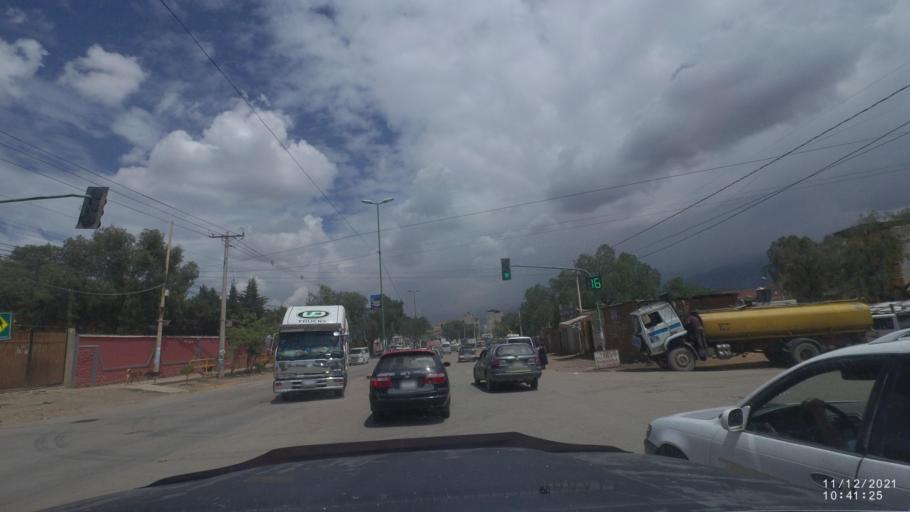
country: BO
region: Cochabamba
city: Cochabamba
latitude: -17.4289
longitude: -66.1290
